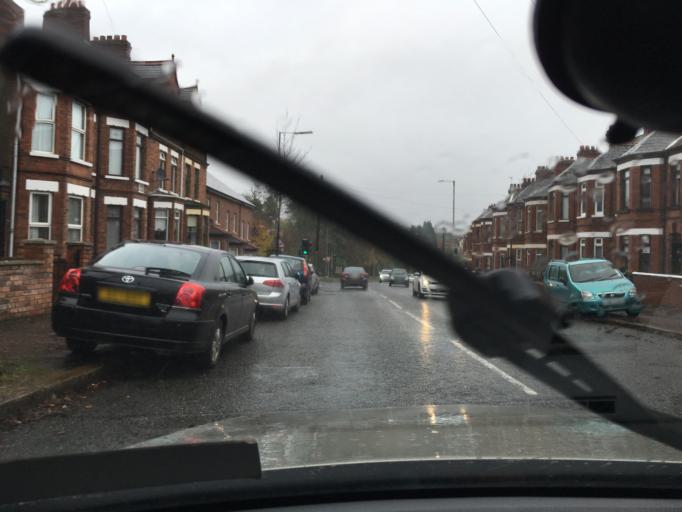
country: GB
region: Northern Ireland
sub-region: City of Belfast
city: Belfast
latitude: 54.6088
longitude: -5.9726
